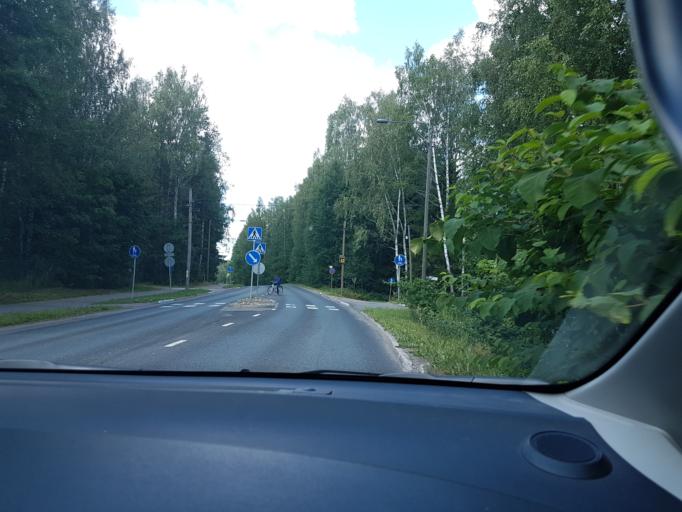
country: FI
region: Uusimaa
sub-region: Helsinki
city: Vantaa
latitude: 60.2595
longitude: 25.1009
